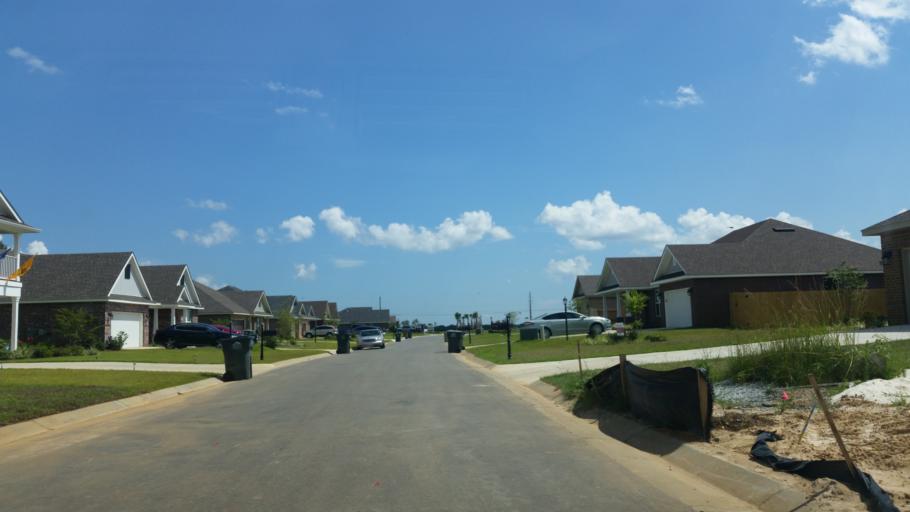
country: US
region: Florida
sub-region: Escambia County
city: Cantonment
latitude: 30.5521
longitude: -87.3701
